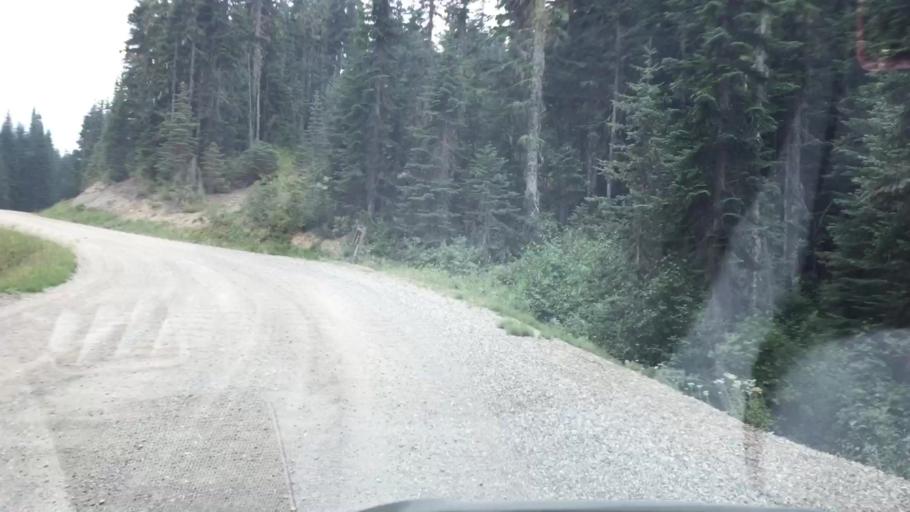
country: US
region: Washington
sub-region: Klickitat County
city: White Salmon
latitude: 46.2698
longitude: -121.6044
